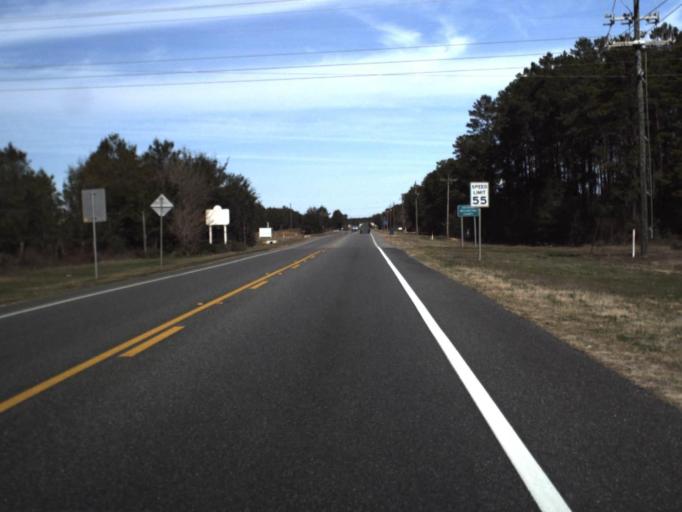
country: US
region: Florida
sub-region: Bay County
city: Lynn Haven
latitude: 30.4386
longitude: -85.6881
